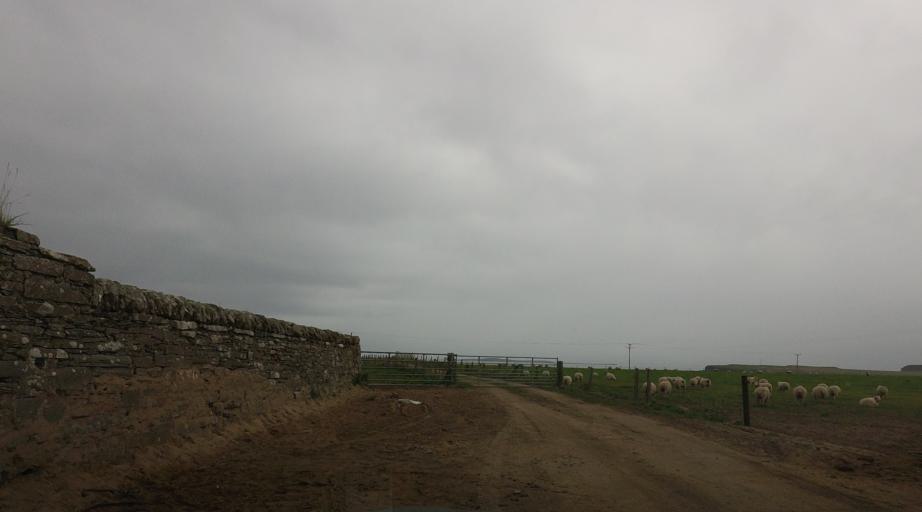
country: GB
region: Scotland
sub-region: Orkney Islands
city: Orkney
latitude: 58.7341
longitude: -2.9588
